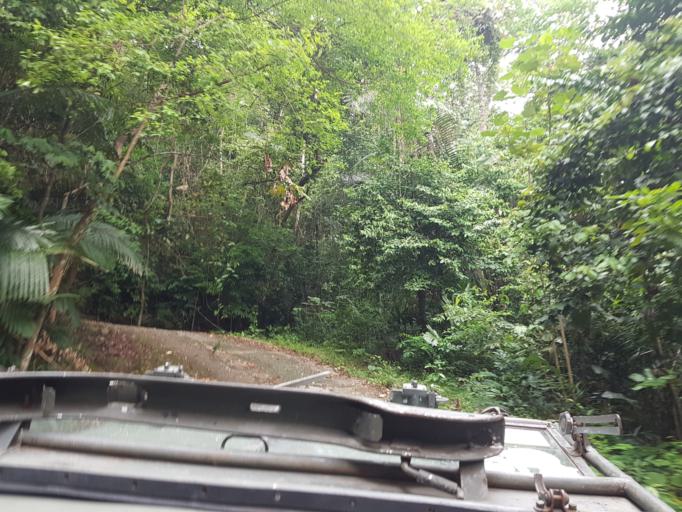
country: TH
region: Pattani
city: Khok Pho
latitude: 6.6549
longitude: 101.0994
